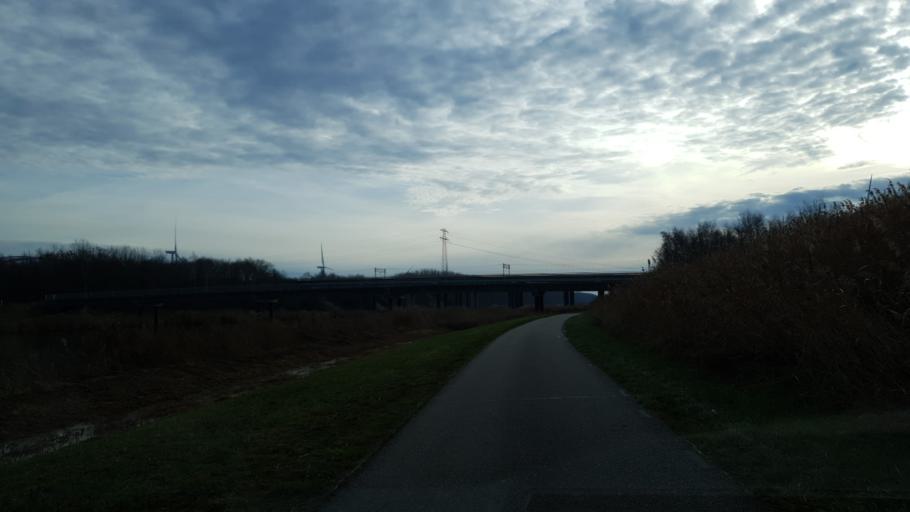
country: NL
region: North Brabant
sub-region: Gemeente Woensdrecht
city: Woensdrecht
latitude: 51.4309
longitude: 4.2290
